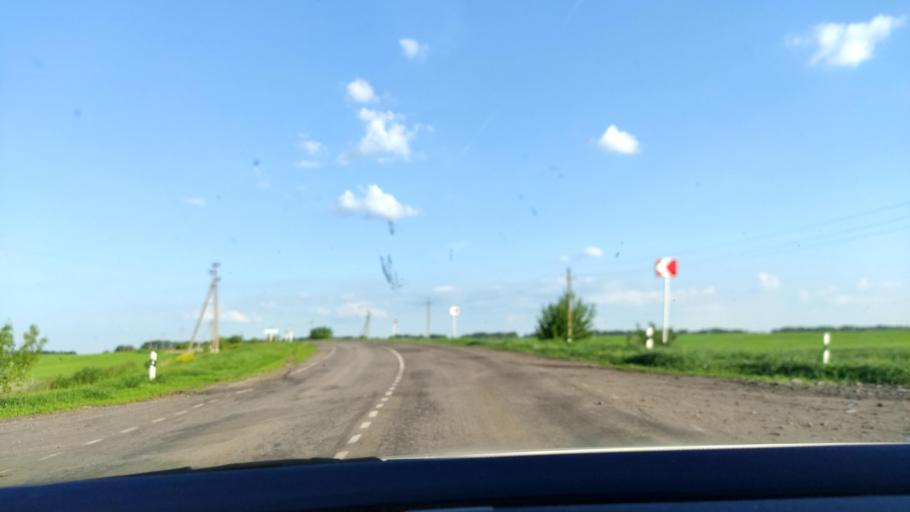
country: RU
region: Voronezj
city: Kashirskoye
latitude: 51.4975
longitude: 39.8350
